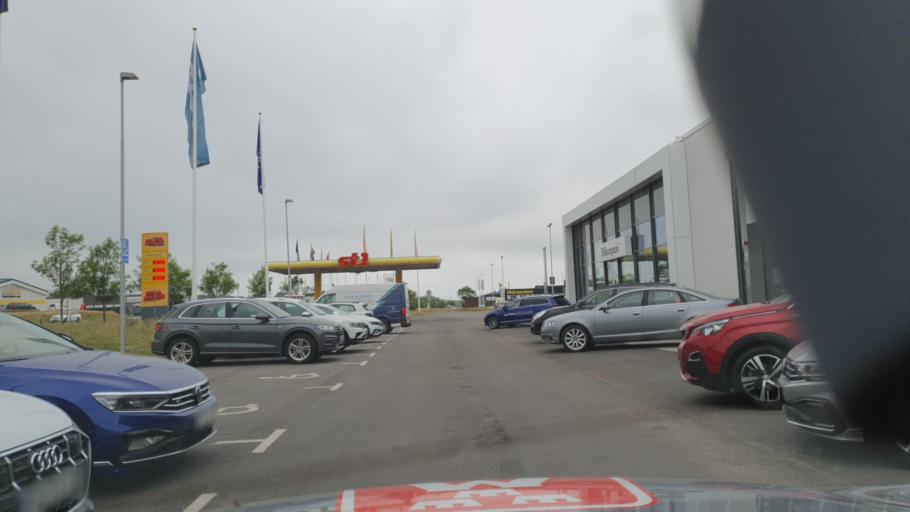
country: SE
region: Kalmar
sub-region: Kalmar Kommun
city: Kalmar
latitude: 56.6954
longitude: 16.3311
